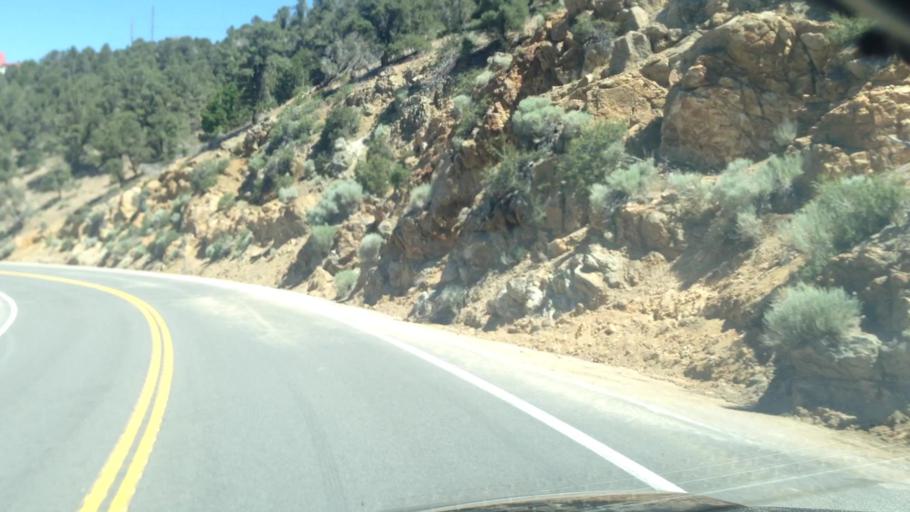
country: US
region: Nevada
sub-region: Storey County
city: Virginia City
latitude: 39.3564
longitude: -119.6619
